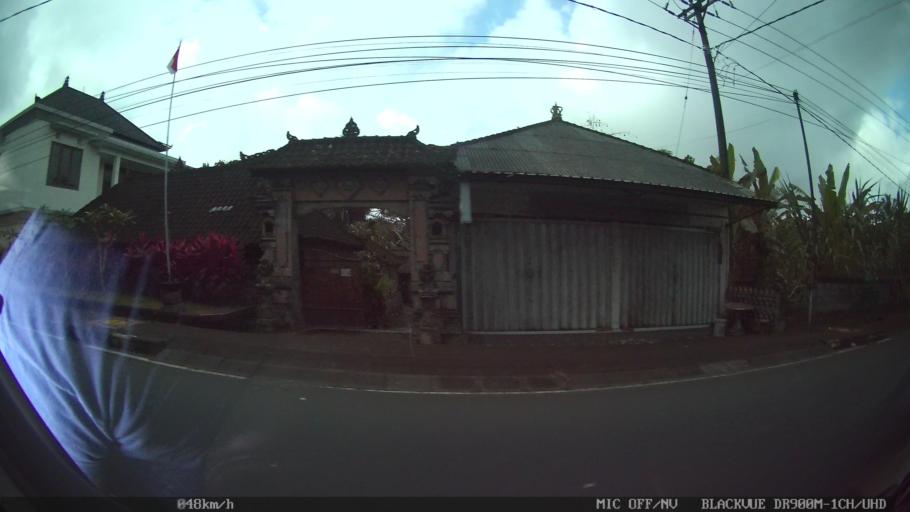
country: ID
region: Bali
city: Petang
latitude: -8.3999
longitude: 115.2186
